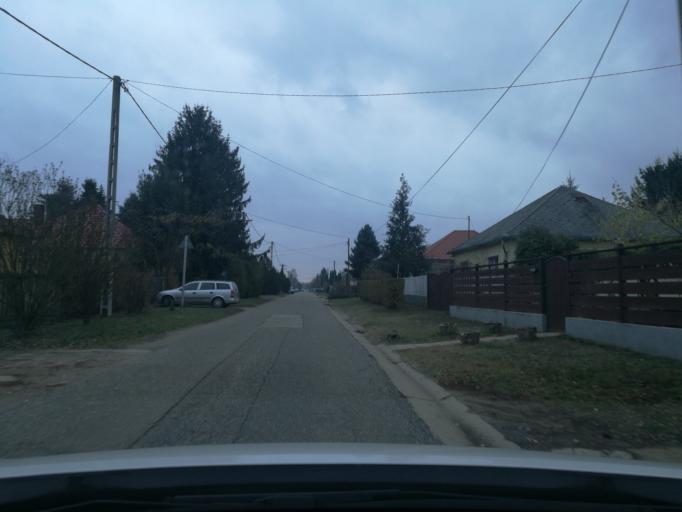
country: HU
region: Szabolcs-Szatmar-Bereg
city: Nyirpazony
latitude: 47.9556
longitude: 21.7828
